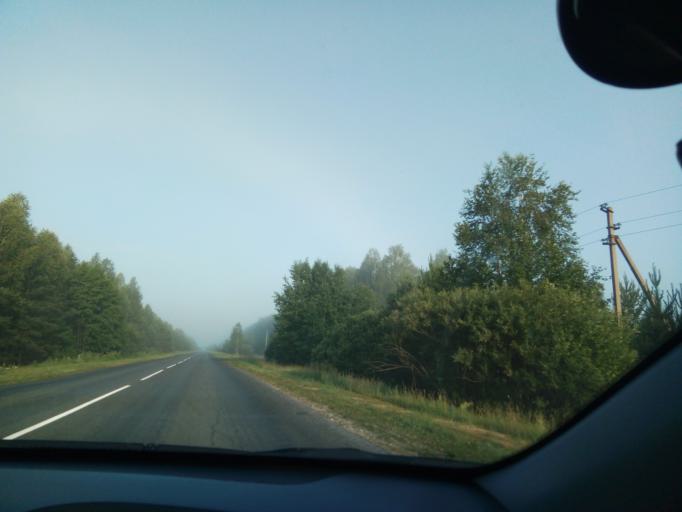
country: RU
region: Nizjnij Novgorod
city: Voznesenskoye
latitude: 54.8625
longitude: 42.9381
